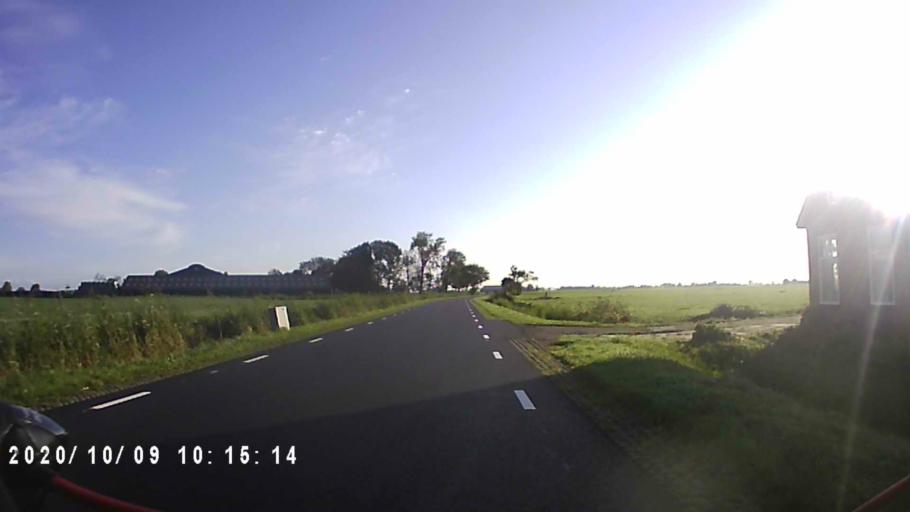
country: NL
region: Groningen
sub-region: Gemeente Winsum
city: Winsum
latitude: 53.3064
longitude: 6.5005
